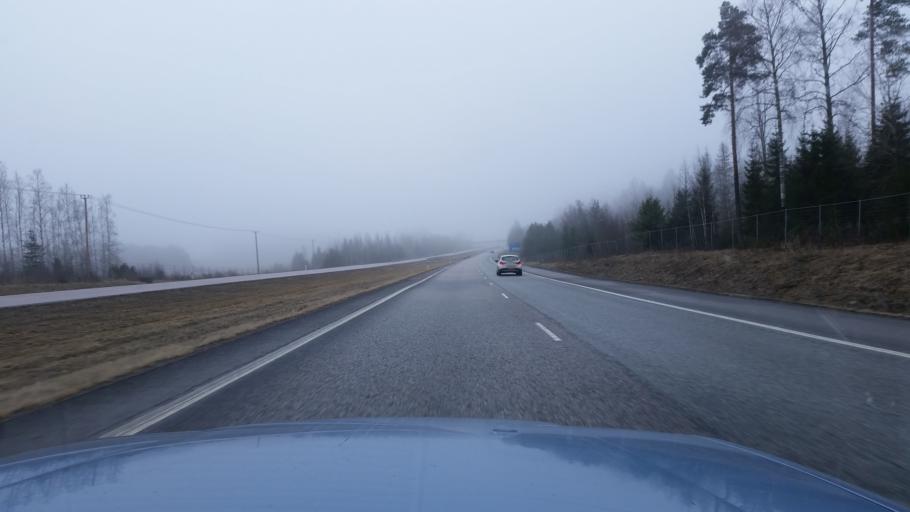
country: FI
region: Uusimaa
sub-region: Helsinki
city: Nurmijaervi
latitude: 60.4699
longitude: 24.8498
